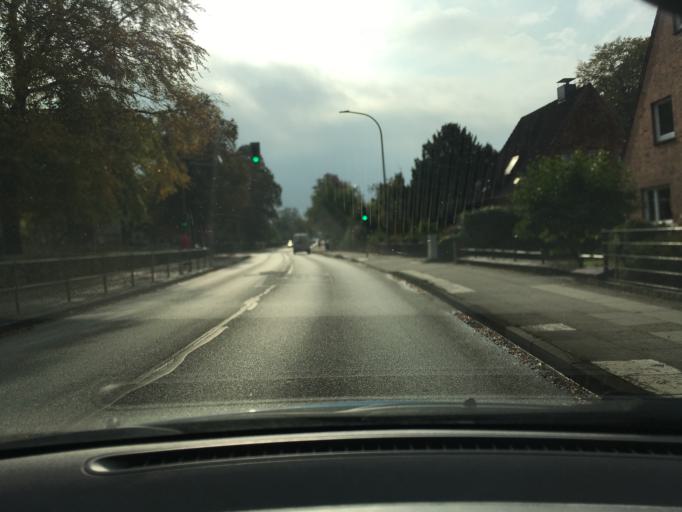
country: DE
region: Schleswig-Holstein
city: Bad Segeberg
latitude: 53.9445
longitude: 10.3013
